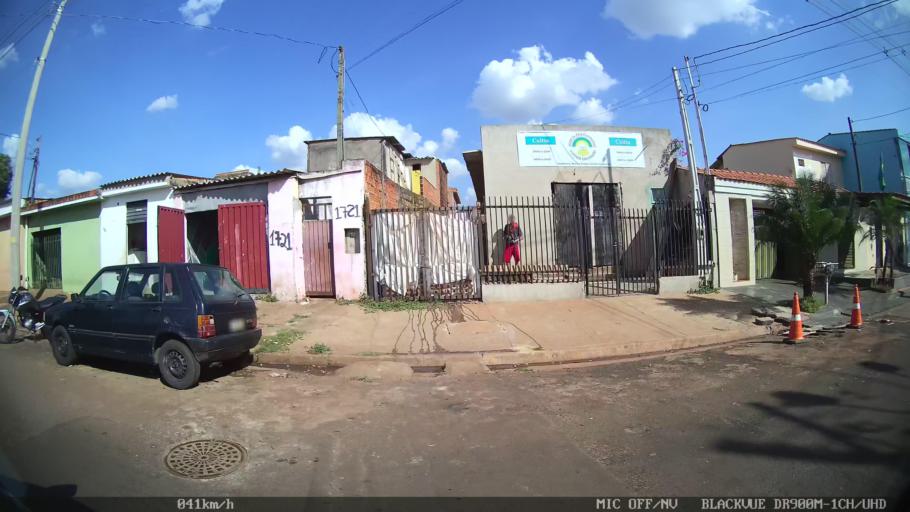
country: BR
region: Sao Paulo
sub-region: Ribeirao Preto
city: Ribeirao Preto
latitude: -21.2039
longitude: -47.8505
